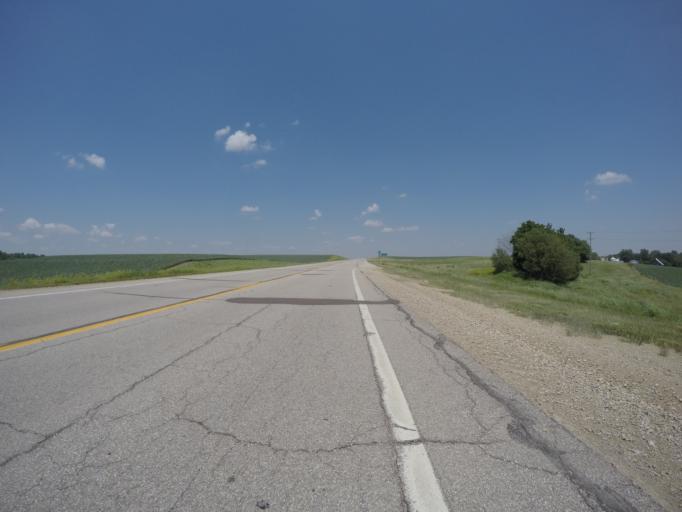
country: US
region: Kansas
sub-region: Doniphan County
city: Troy
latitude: 39.7574
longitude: -95.1437
